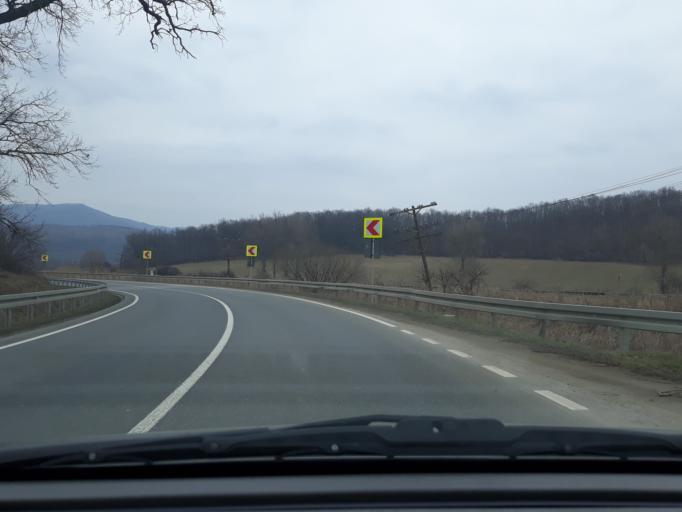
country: RO
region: Salaj
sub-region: Comuna Nusfalau
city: Nusfalau
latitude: 47.2196
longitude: 22.7464
